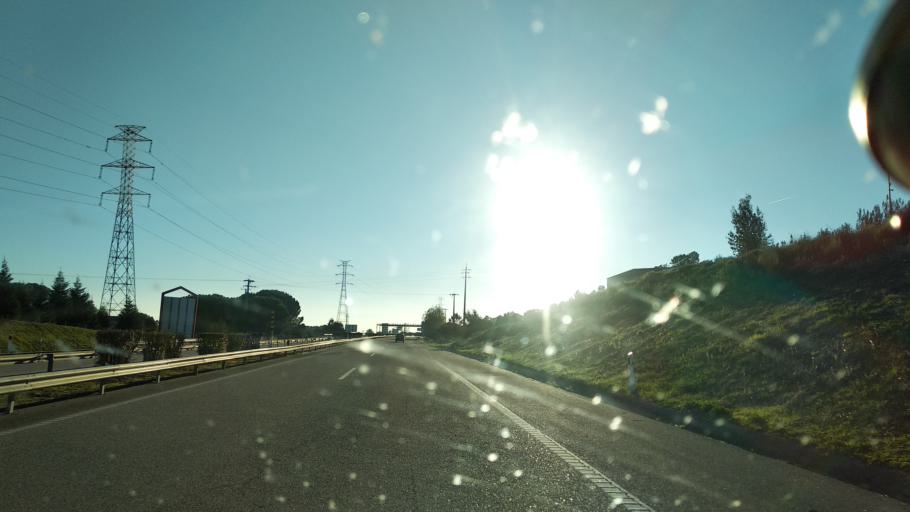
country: PT
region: Santarem
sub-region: Entroncamento
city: Entroncamento
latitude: 39.4831
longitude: -8.4768
